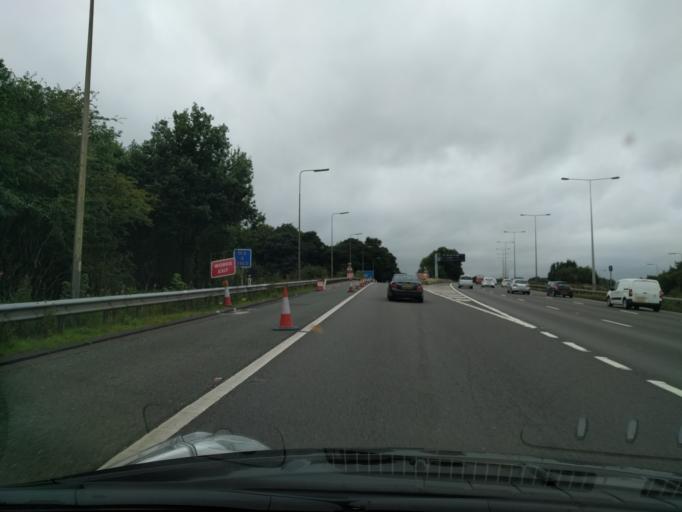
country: GB
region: England
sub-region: Borough of Wigan
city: Ashton in Makerfield
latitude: 53.4686
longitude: -2.6318
